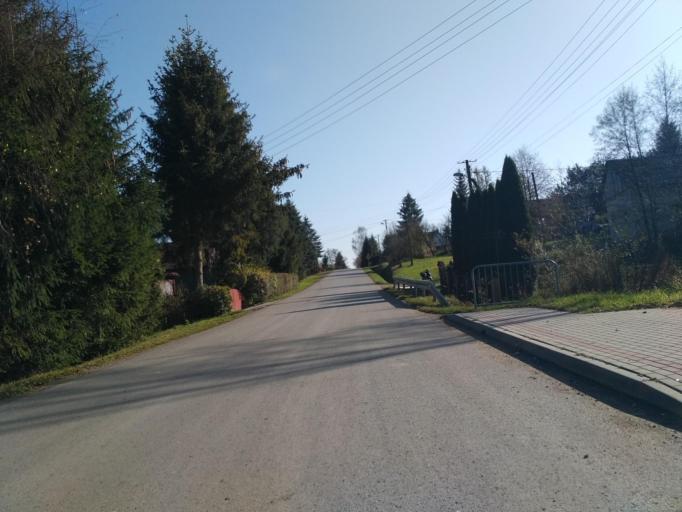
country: PL
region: Subcarpathian Voivodeship
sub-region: Powiat brzozowski
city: Nozdrzec
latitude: 49.8039
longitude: 22.1682
